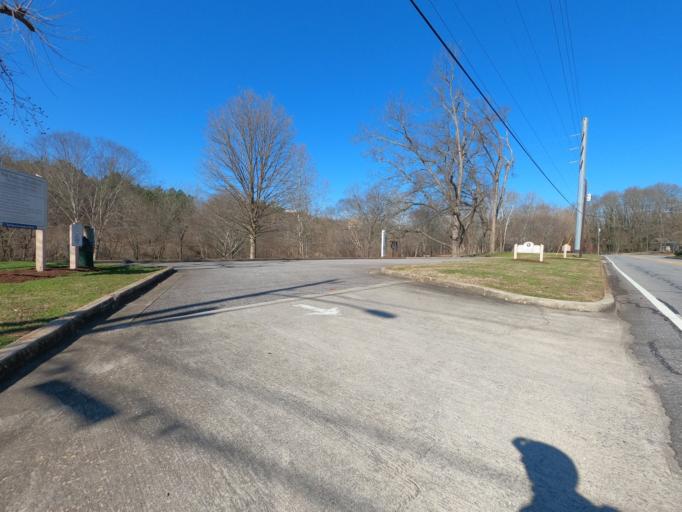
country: US
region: Georgia
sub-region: Clarke County
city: Athens
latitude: 33.9622
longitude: -83.3685
